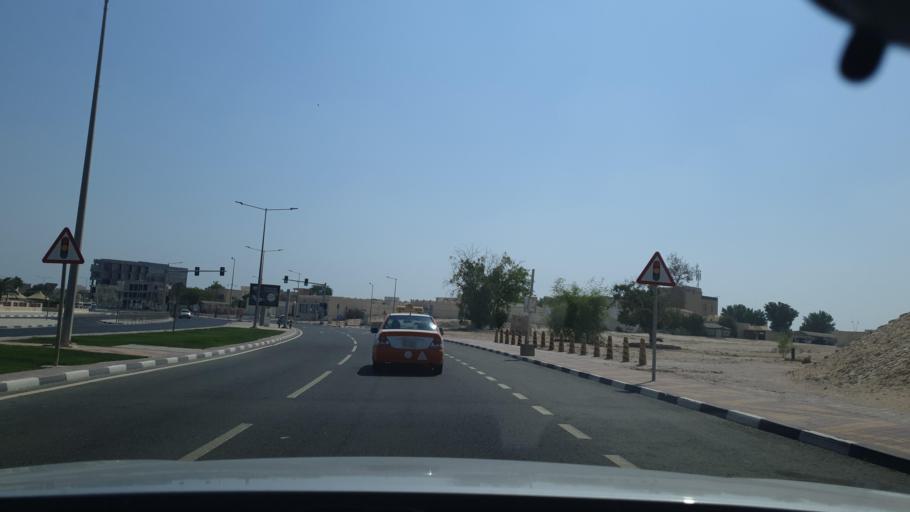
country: QA
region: Al Khawr
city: Al Khawr
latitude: 25.6869
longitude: 51.5080
